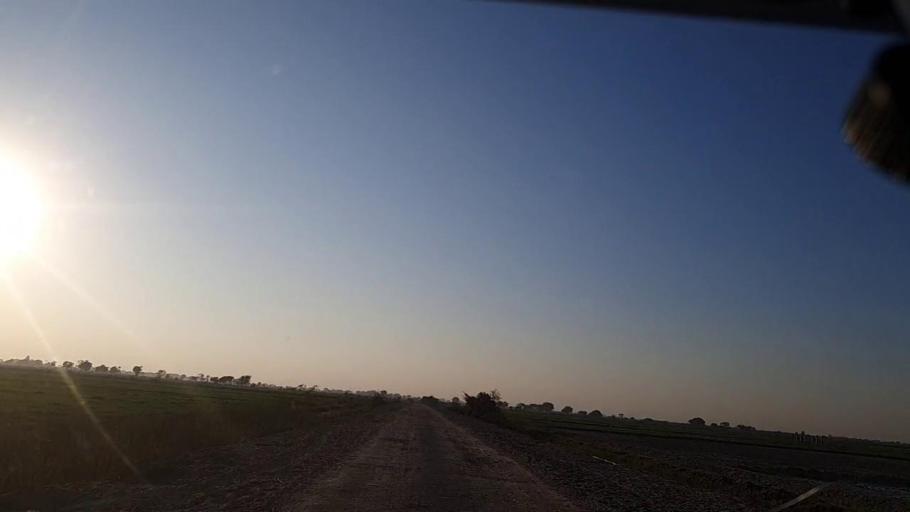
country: PK
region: Sindh
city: Khanpur
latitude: 27.7904
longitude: 69.3145
